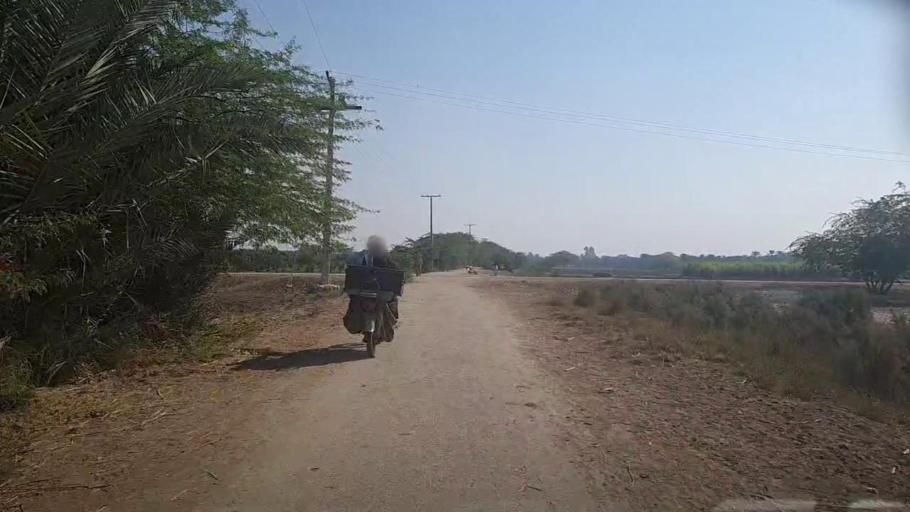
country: PK
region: Sindh
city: Kot Diji
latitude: 27.4376
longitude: 68.7118
